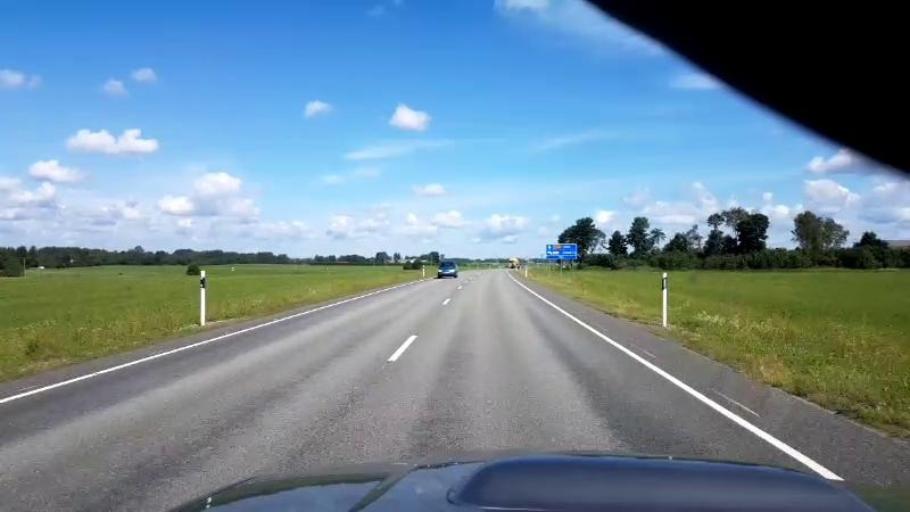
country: EE
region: Jaervamaa
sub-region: Jaerva-Jaani vald
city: Jarva-Jaani
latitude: 59.1677
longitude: 25.7582
